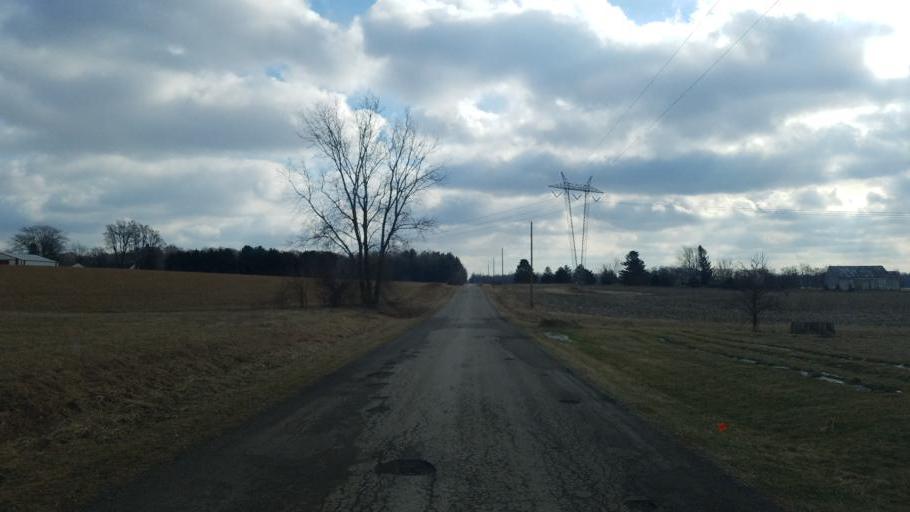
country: US
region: Ohio
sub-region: Crawford County
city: Galion
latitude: 40.6659
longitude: -82.7467
